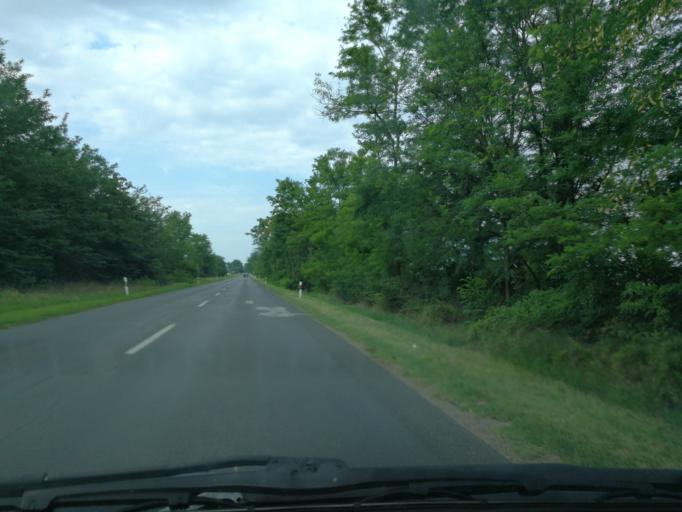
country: HU
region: Bacs-Kiskun
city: Ersekcsanad
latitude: 46.2283
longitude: 18.9704
